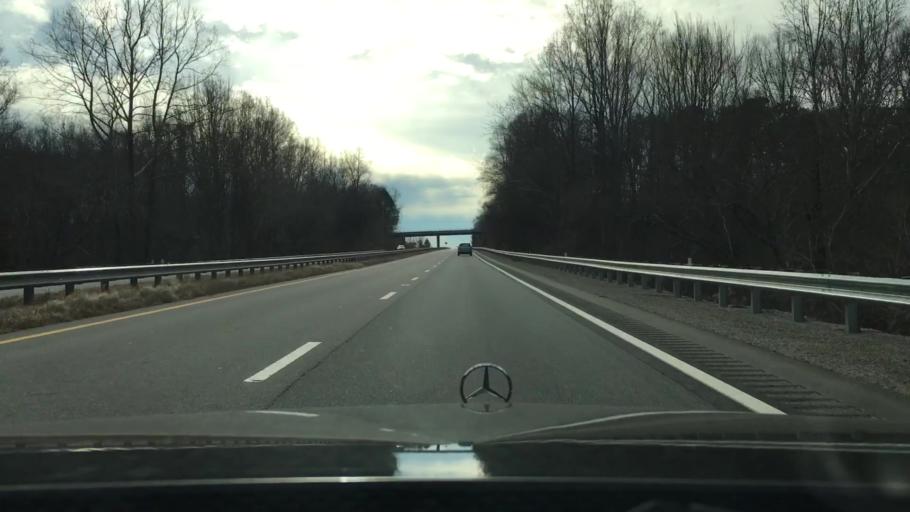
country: US
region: Virginia
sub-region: Pittsylvania County
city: Chatham
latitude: 36.8133
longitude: -79.3860
